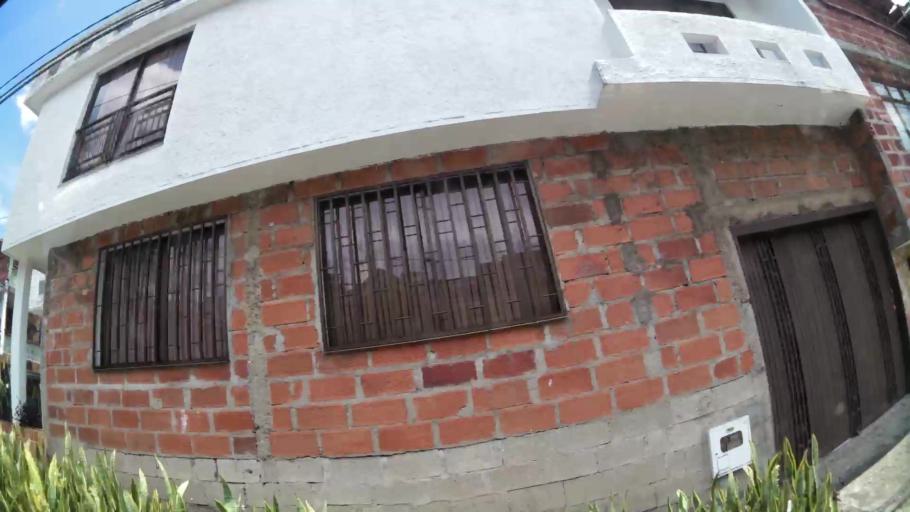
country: CO
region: Antioquia
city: La Estrella
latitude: 6.1599
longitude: -75.6418
